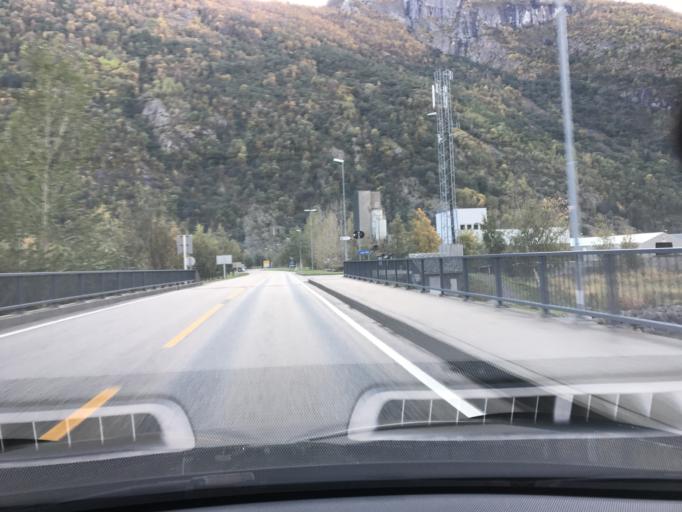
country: NO
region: Sogn og Fjordane
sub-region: Laerdal
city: Laerdalsoyri
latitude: 61.1020
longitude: 7.4759
